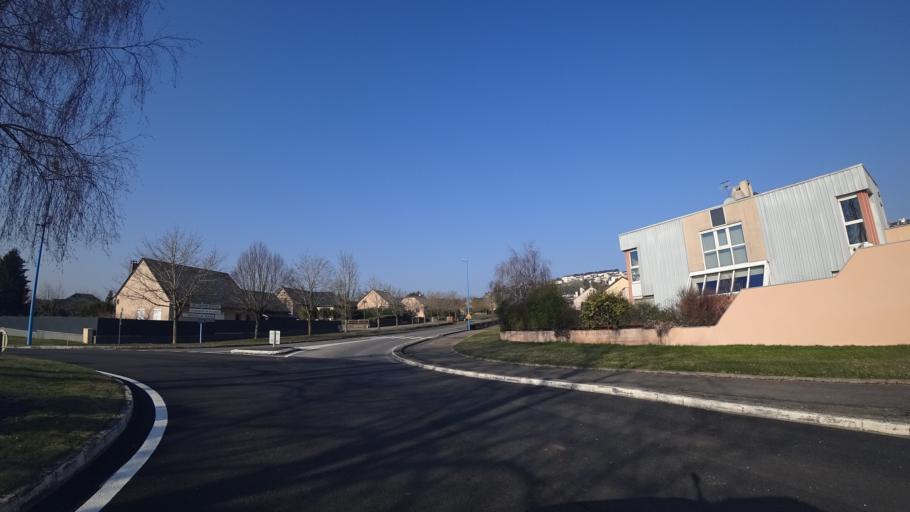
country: FR
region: Midi-Pyrenees
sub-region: Departement de l'Aveyron
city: Rodez
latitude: 44.3730
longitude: 2.5775
